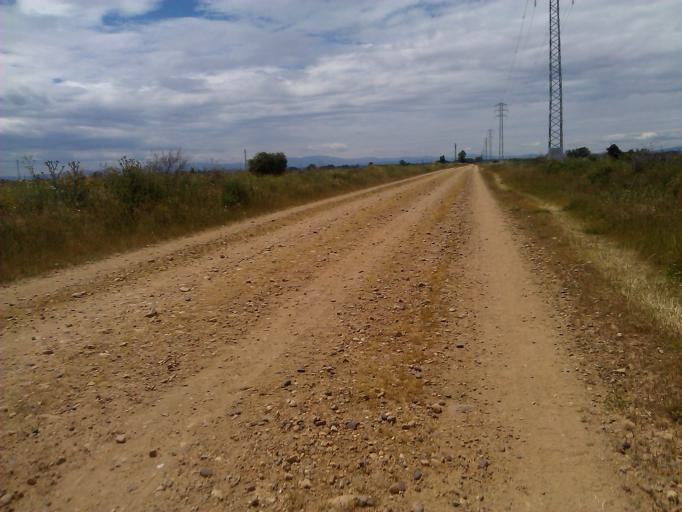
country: ES
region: Castille and Leon
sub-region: Provincia de Leon
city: Bustillo del Paramo
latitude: 42.4604
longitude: -5.8154
